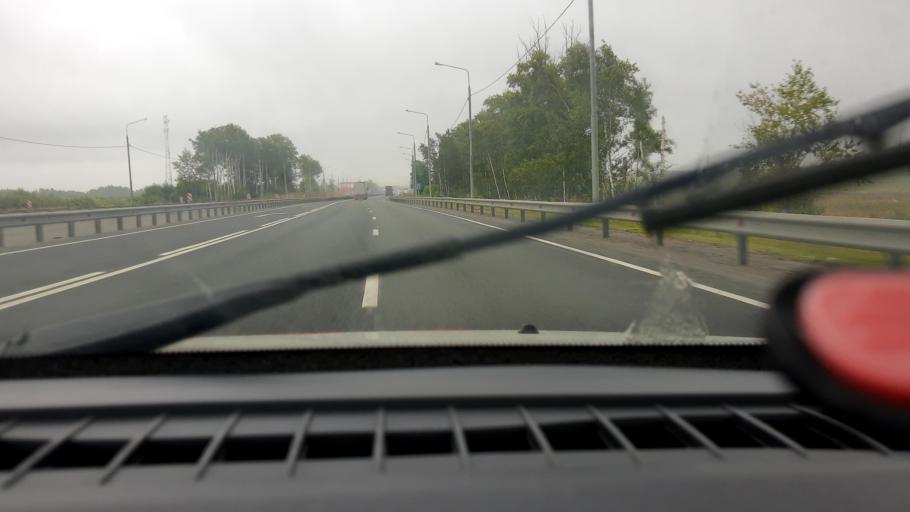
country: RU
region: Vladimir
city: Novovyazniki
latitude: 56.2031
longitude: 42.3027
